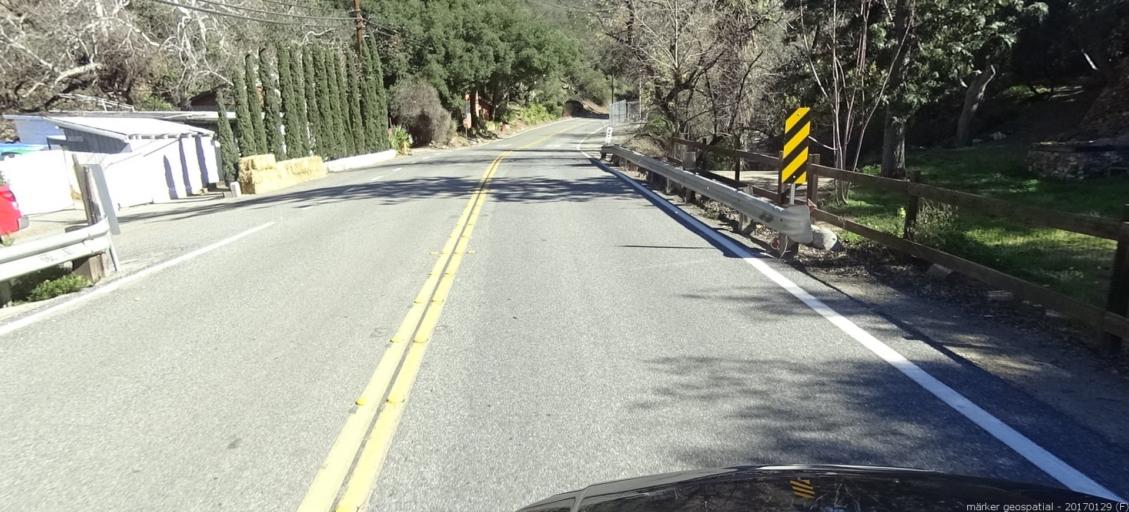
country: US
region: California
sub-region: Orange County
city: Portola Hills
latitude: 33.7469
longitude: -117.6262
